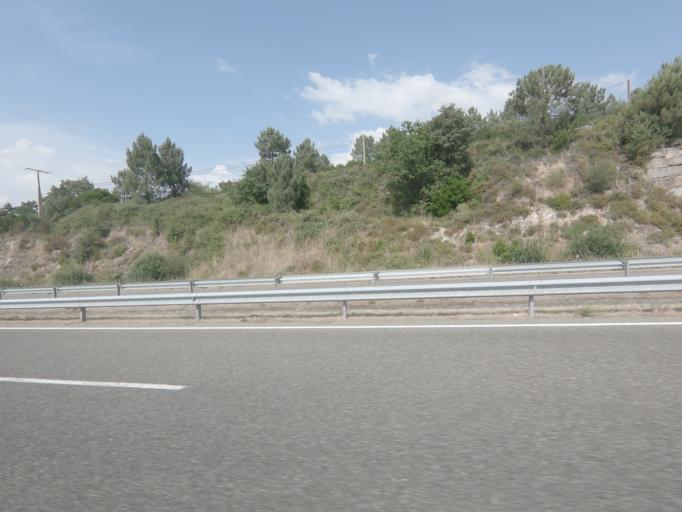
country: ES
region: Galicia
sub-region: Provincia de Ourense
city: Ourense
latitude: 42.2840
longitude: -7.8742
